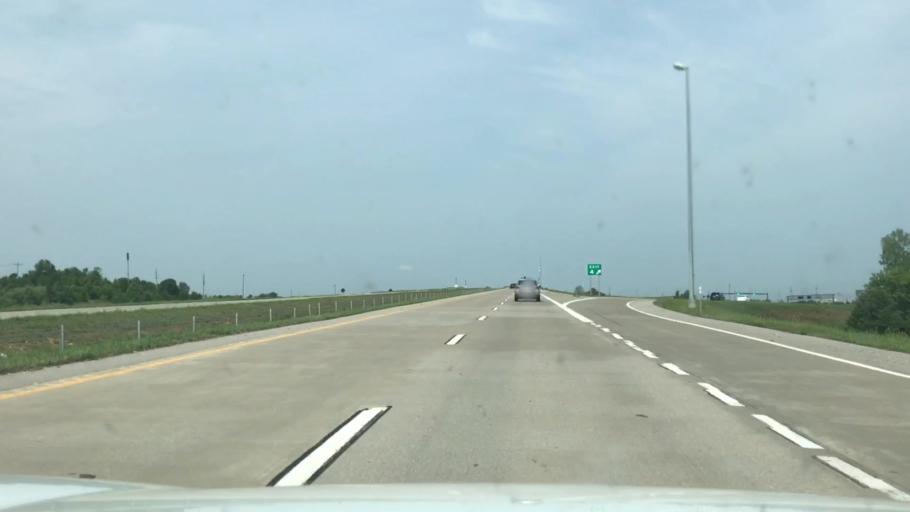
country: US
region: Missouri
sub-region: Saint Charles County
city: Dardenne Prairie
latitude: 38.7522
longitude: -90.6956
